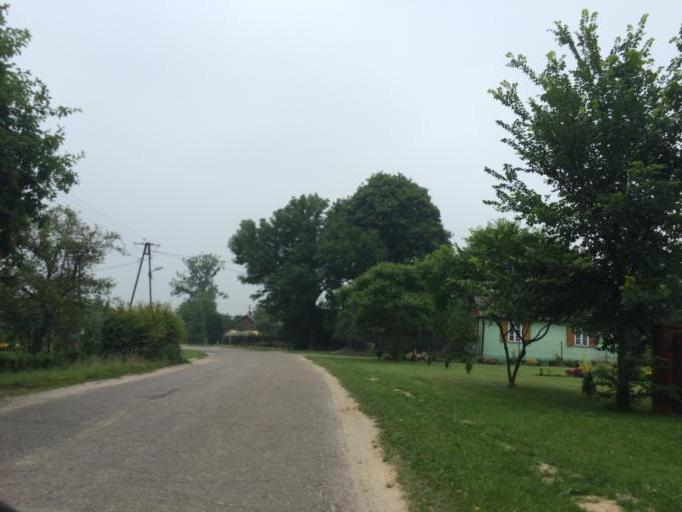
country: PL
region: Lublin Voivodeship
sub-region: Powiat pulawski
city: Markuszow
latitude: 51.3614
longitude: 22.2581
